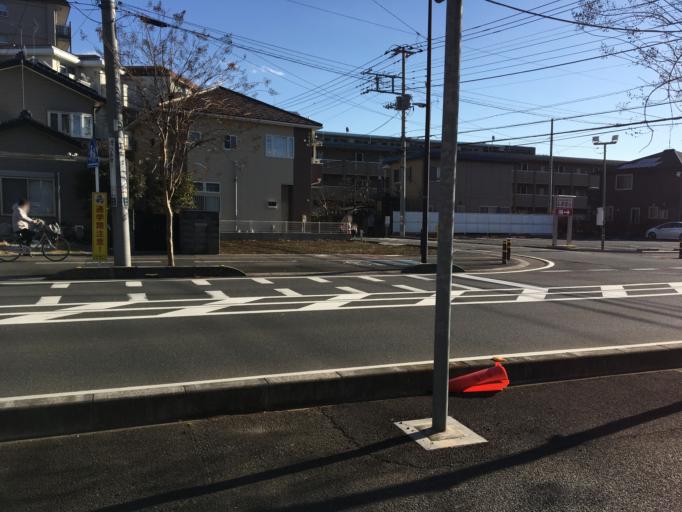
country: JP
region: Saitama
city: Oi
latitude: 35.8409
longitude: 139.5326
